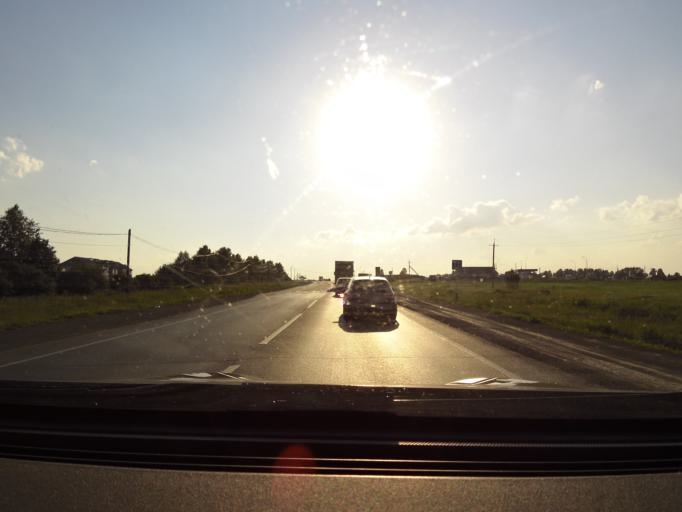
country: RU
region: Sverdlovsk
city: Druzhinino
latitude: 56.8105
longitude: 59.5316
